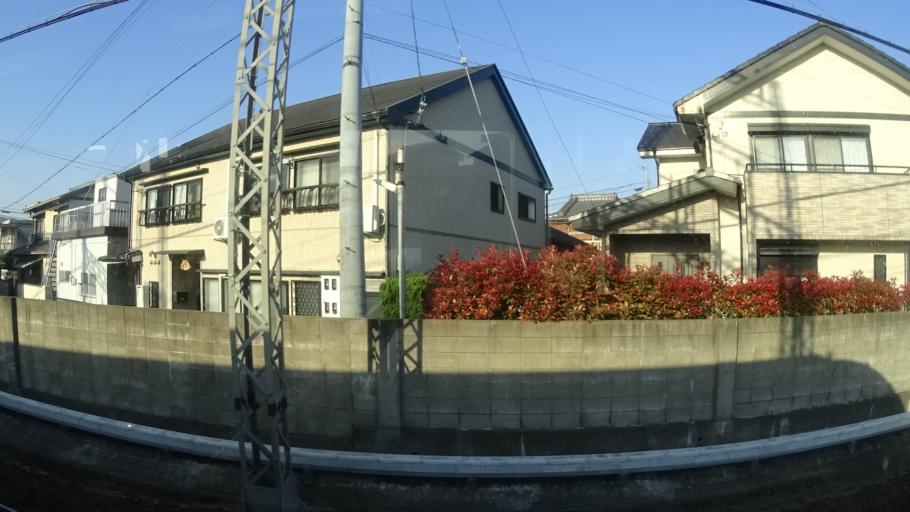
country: JP
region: Mie
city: Ise
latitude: 34.4990
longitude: 136.6970
